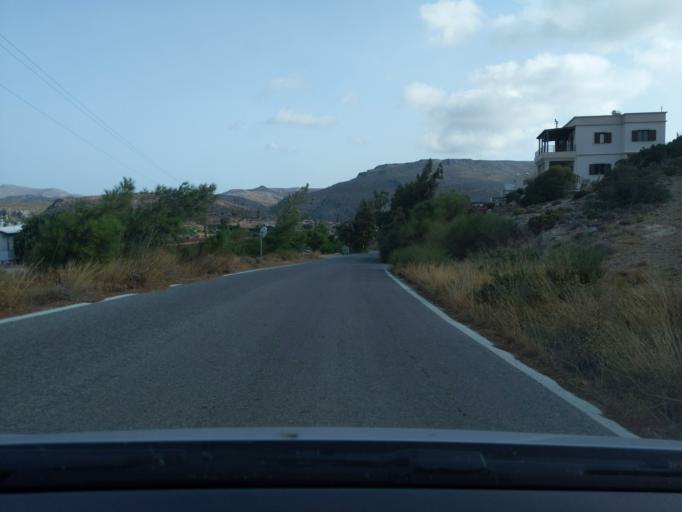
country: GR
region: Crete
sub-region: Nomos Lasithiou
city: Palekastro
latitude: 35.0950
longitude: 26.2345
